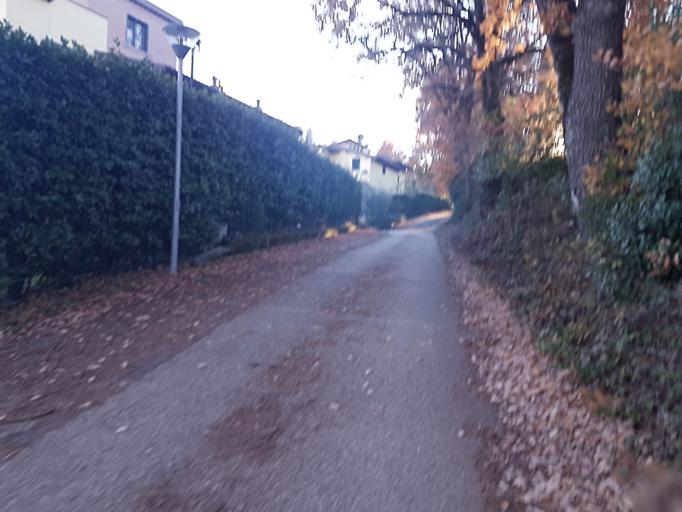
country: IT
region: Umbria
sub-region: Provincia di Perugia
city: Perugia
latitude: 43.0919
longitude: 12.3787
